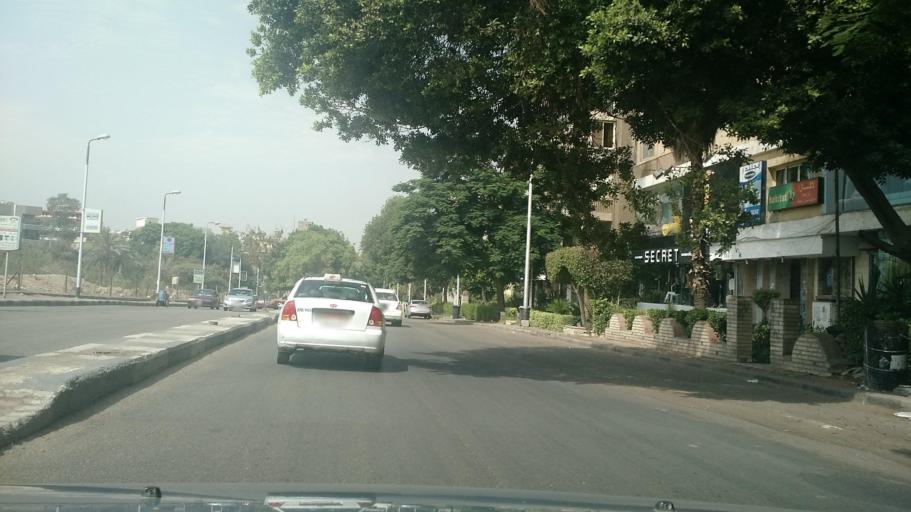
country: EG
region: Al Jizah
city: Al Hawamidiyah
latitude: 29.9655
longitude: 31.2772
